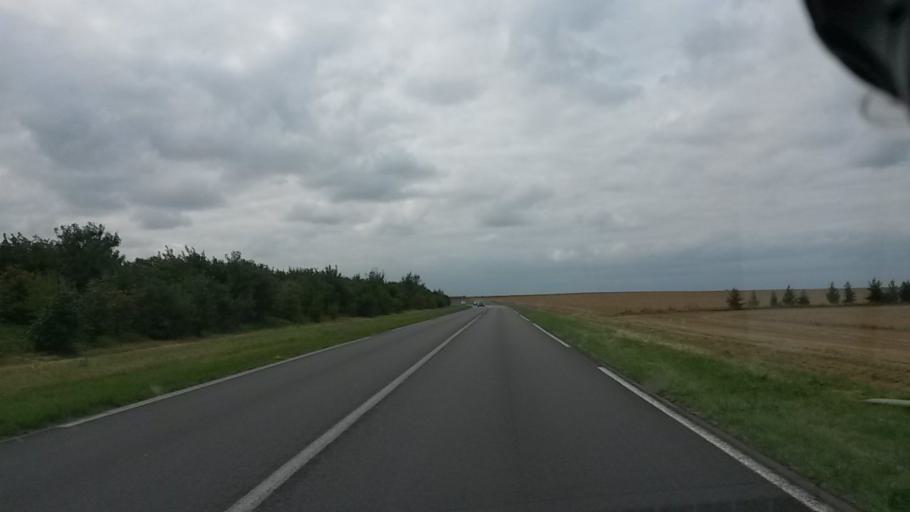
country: FR
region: Picardie
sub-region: Departement de la Somme
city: Corbie
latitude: 49.9570
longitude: 2.4876
